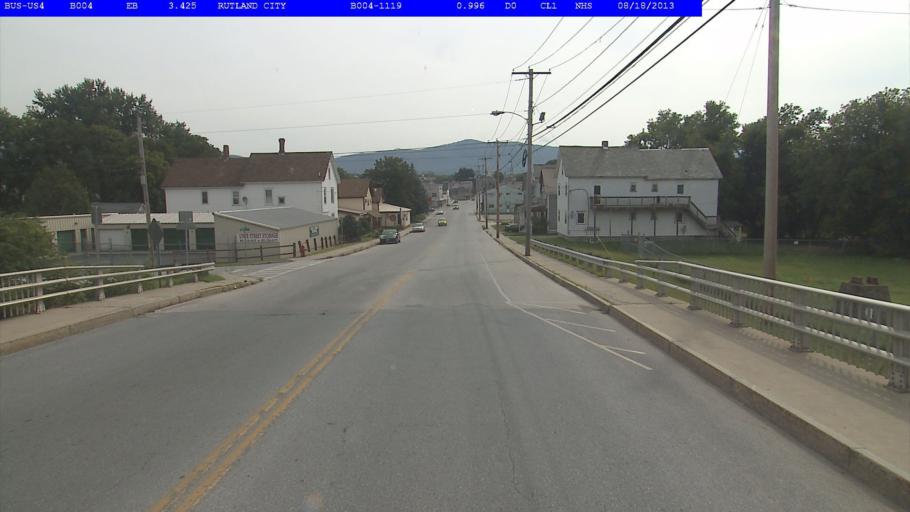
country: US
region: Vermont
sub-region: Rutland County
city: Rutland
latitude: 43.6086
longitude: -72.9894
